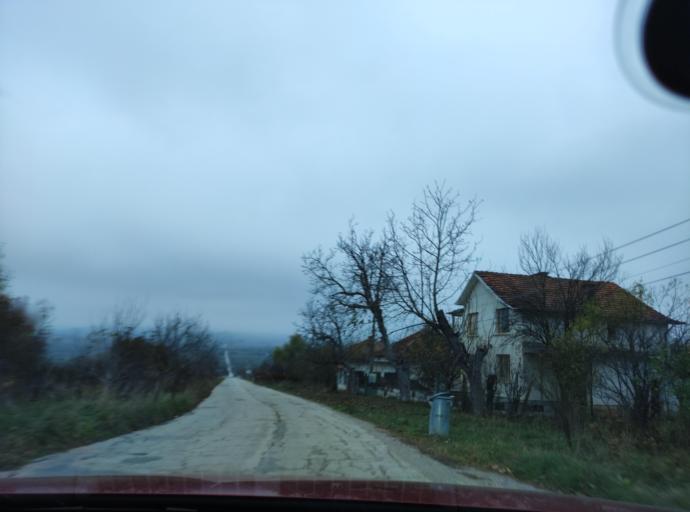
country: BG
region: Lovech
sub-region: Obshtina Yablanitsa
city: Yablanitsa
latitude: 43.0904
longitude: 24.0798
